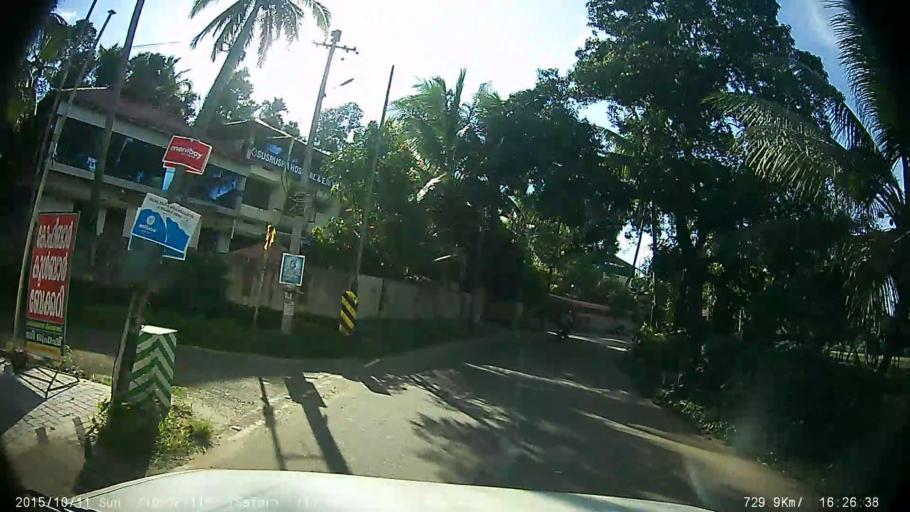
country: IN
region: Kerala
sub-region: Kottayam
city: Palackattumala
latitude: 9.7616
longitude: 76.5684
